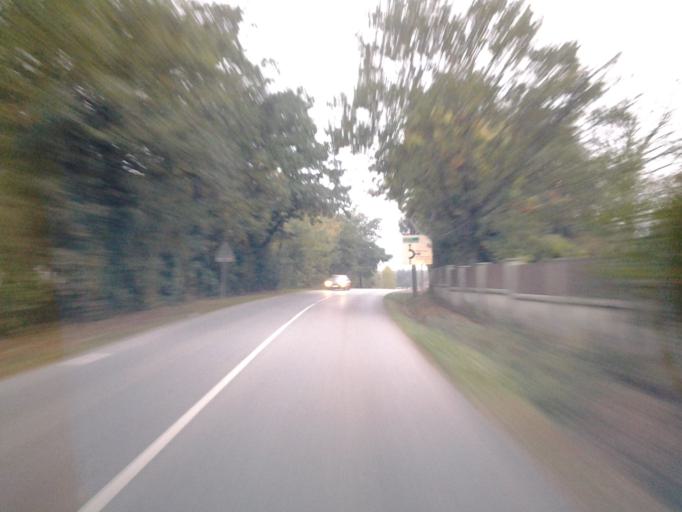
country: FR
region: Pays de la Loire
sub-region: Departement de la Vendee
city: La Roche-sur-Yon
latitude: 46.6454
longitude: -1.4304
